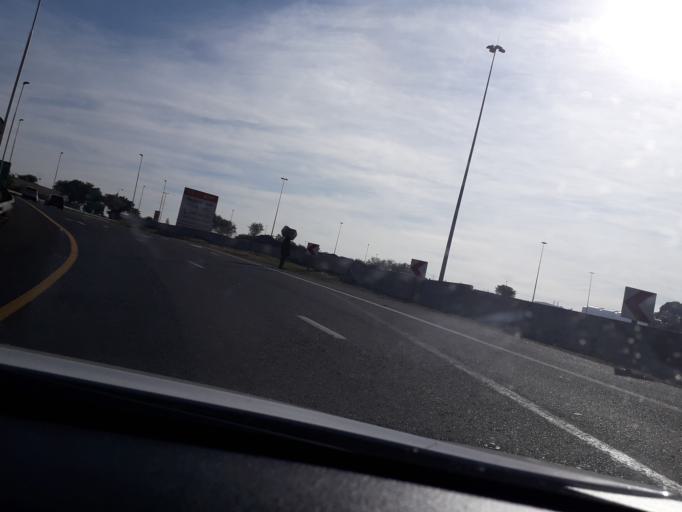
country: ZA
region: Gauteng
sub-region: Ekurhuleni Metropolitan Municipality
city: Germiston
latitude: -26.1627
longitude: 28.1648
